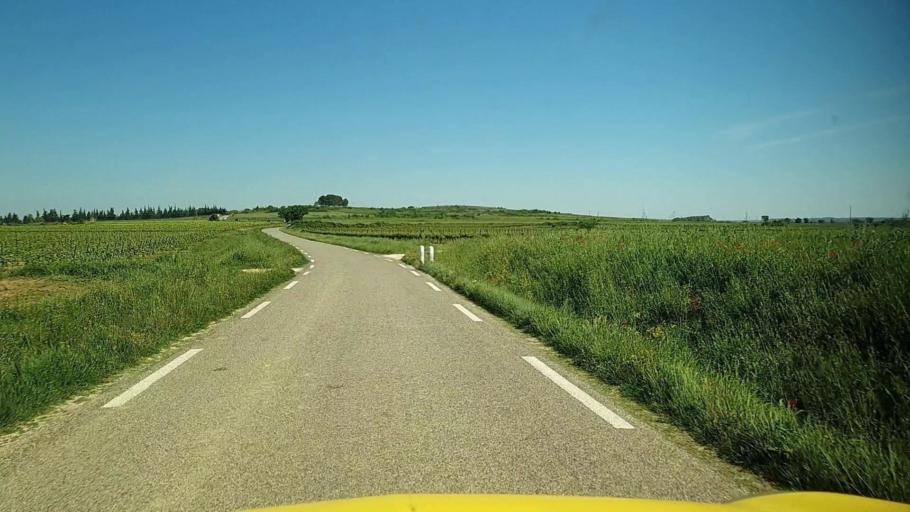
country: FR
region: Languedoc-Roussillon
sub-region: Departement du Gard
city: Saint-Chaptes
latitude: 43.9458
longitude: 4.3089
